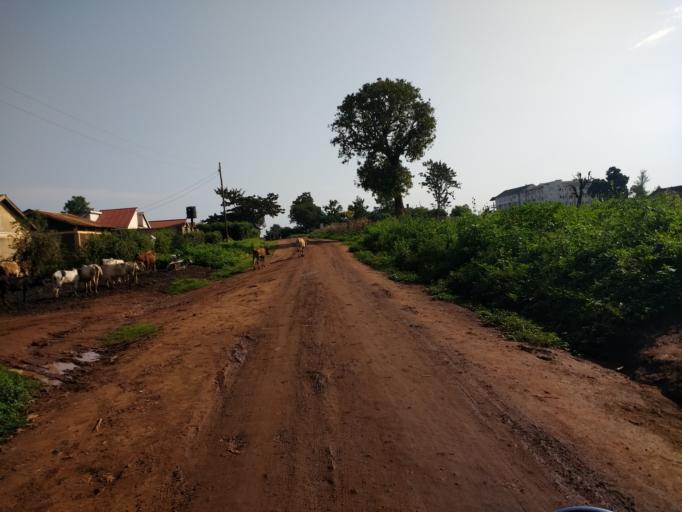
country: UG
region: Eastern Region
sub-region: Mbale District
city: Mbale
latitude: 1.0676
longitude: 34.1640
